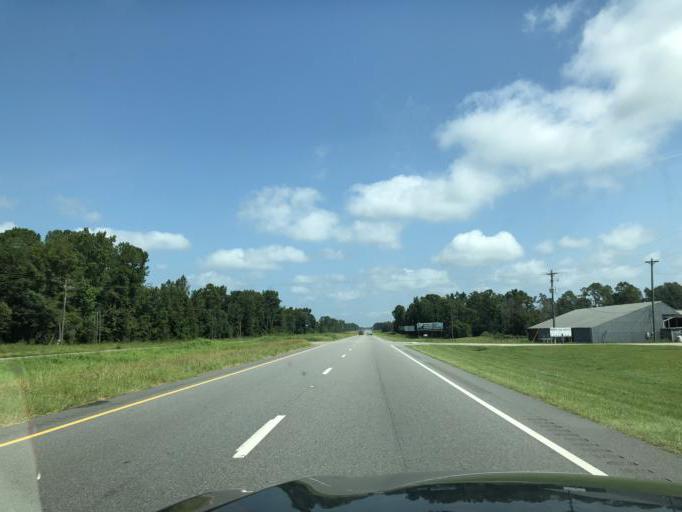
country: US
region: Alabama
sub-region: Houston County
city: Cottonwood
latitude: 31.0207
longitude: -85.4072
